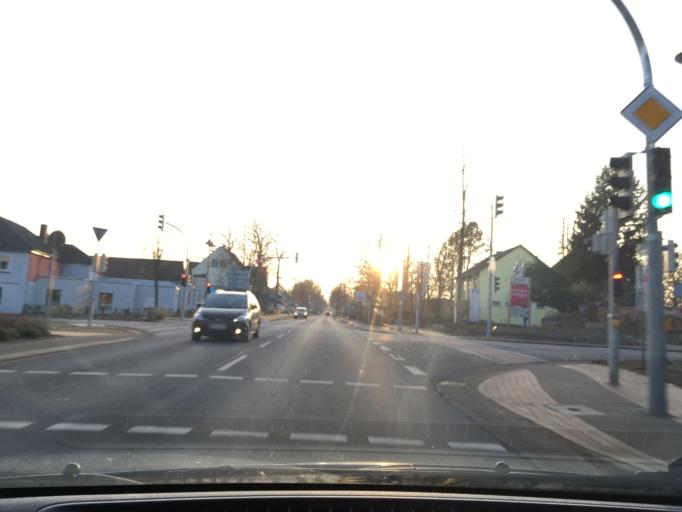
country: DE
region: Lower Saxony
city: Eschede
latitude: 52.7342
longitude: 10.2357
